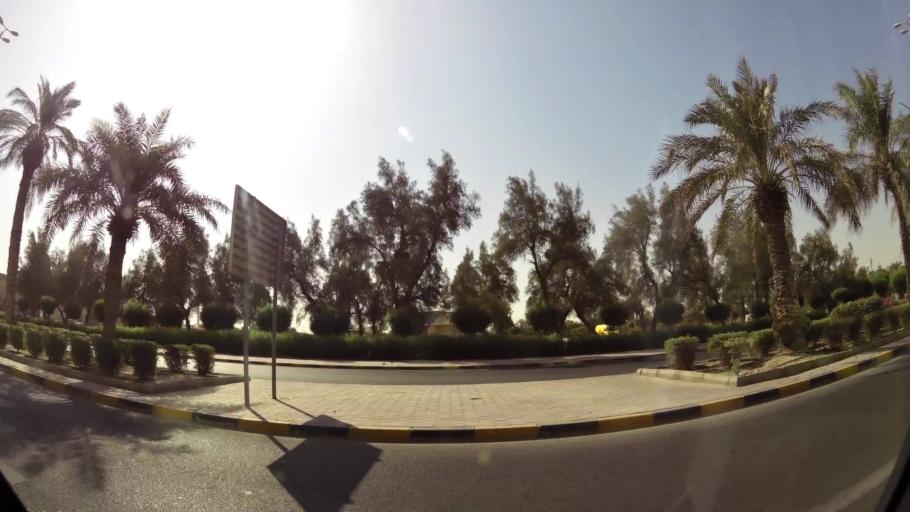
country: KW
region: Al Asimah
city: Kuwait City
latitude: 29.3617
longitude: 47.9800
